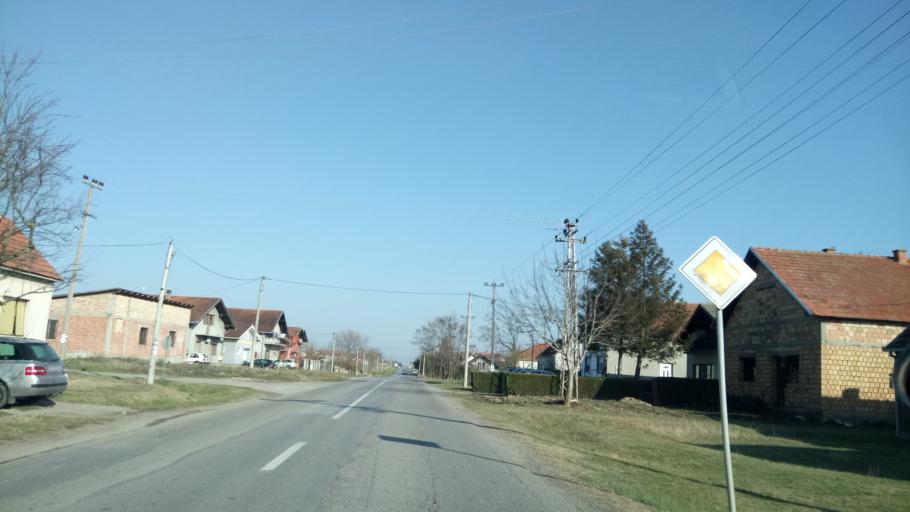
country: RS
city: Ljukovo
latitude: 45.0207
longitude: 20.0351
